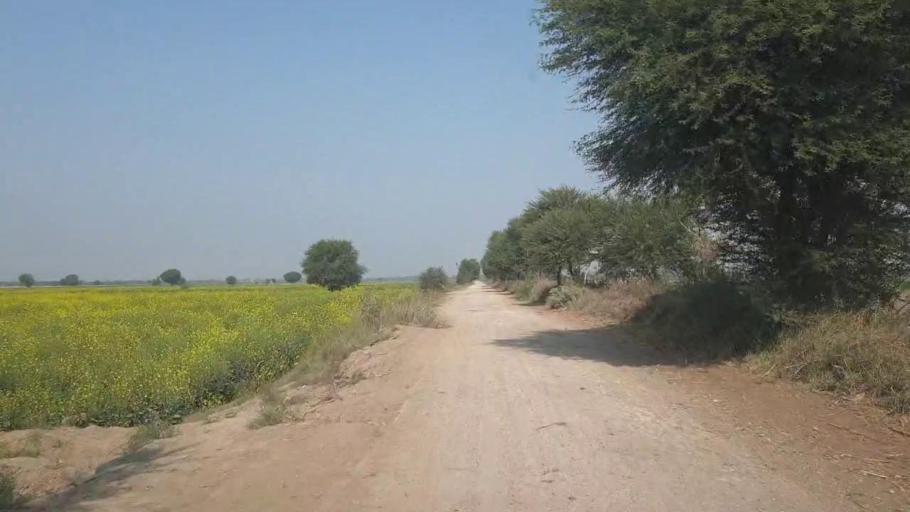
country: PK
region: Sindh
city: Tando Allahyar
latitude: 25.4558
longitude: 68.8319
